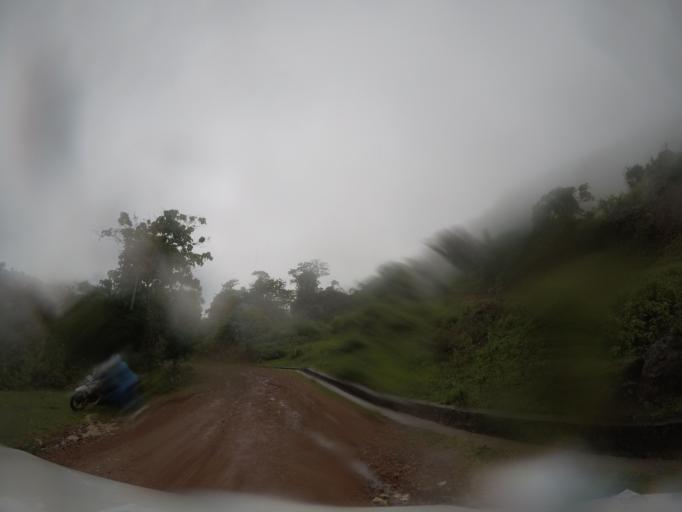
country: TL
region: Baucau
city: Venilale
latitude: -8.6373
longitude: 126.4120
